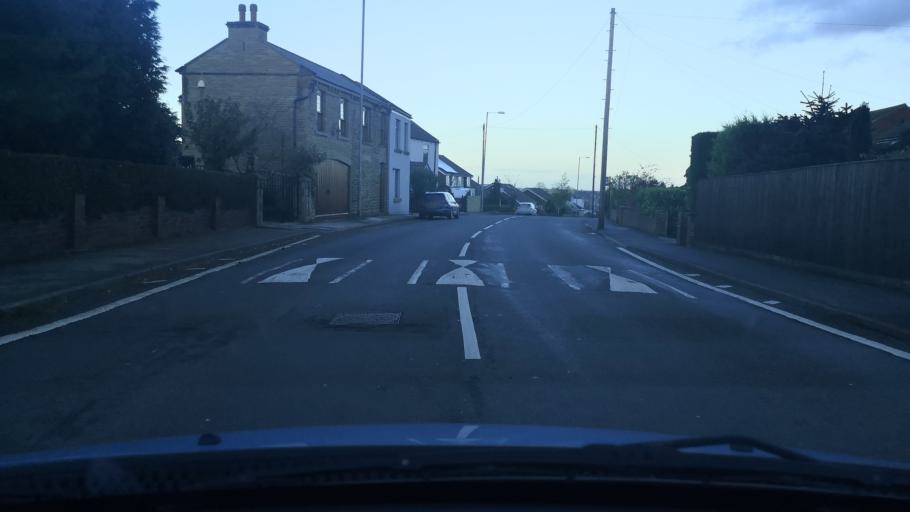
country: GB
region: England
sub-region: City and Borough of Wakefield
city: Middlestown
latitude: 53.6456
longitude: -1.5787
